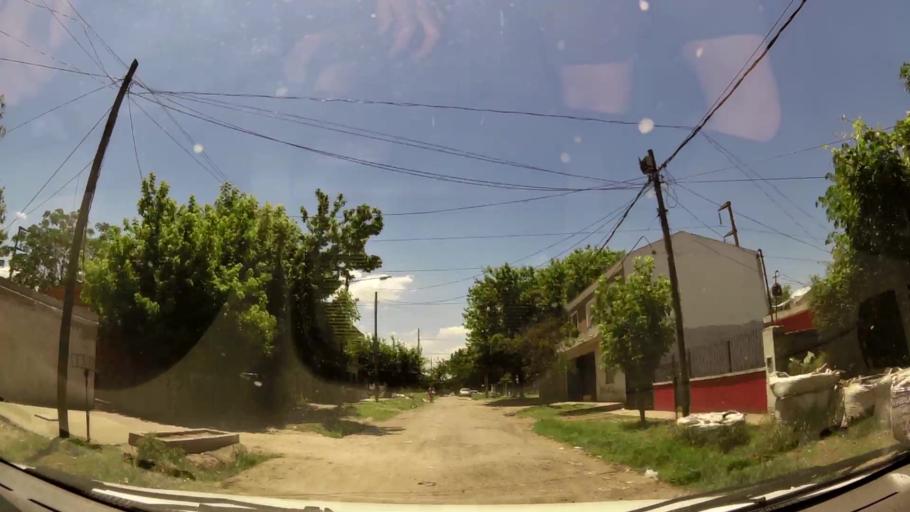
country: AR
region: Buenos Aires
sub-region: Partido de Merlo
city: Merlo
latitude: -34.6499
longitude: -58.7030
